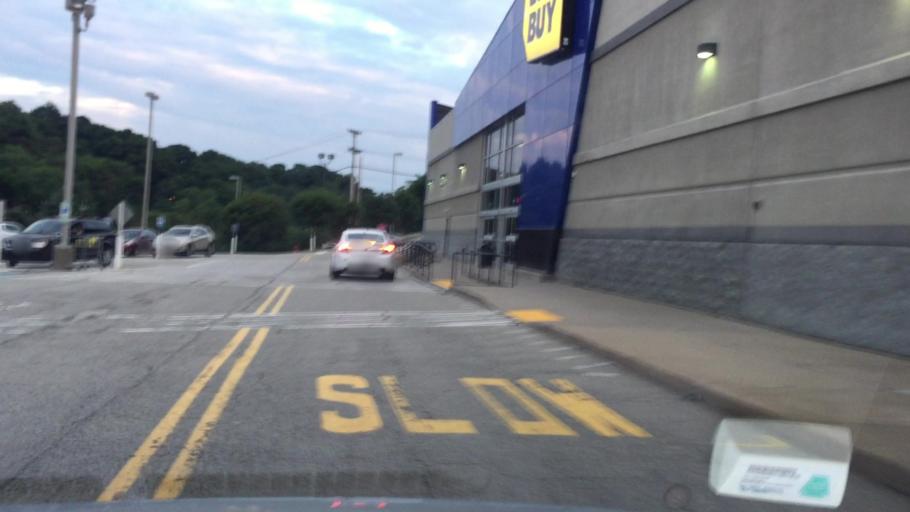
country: US
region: Pennsylvania
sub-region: Allegheny County
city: West View
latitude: 40.5238
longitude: -80.0066
